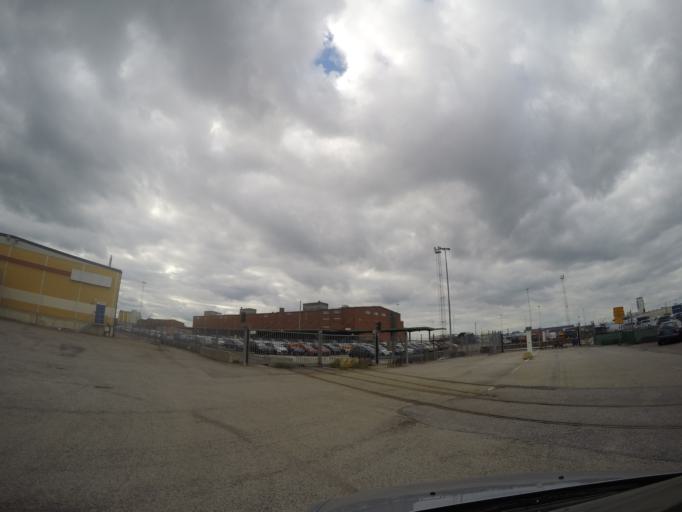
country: SE
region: Skane
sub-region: Malmo
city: Malmoe
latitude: 55.6147
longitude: 13.0139
